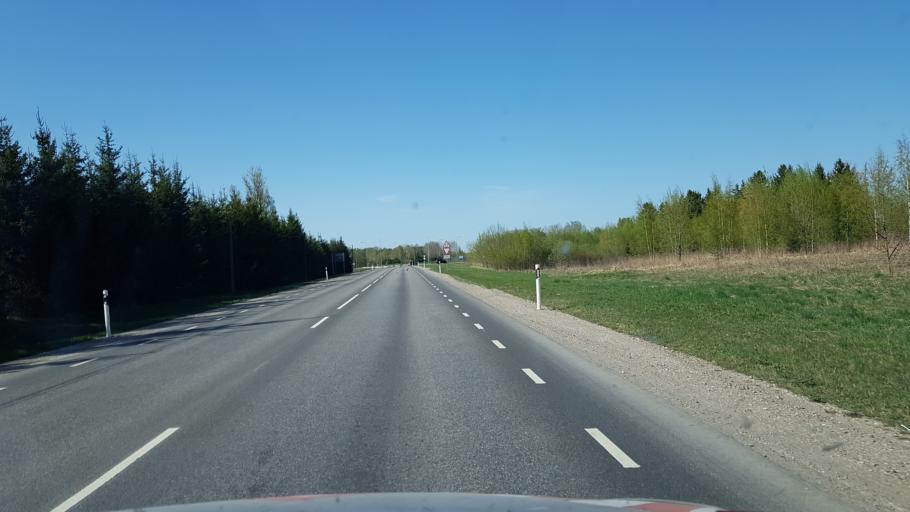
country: EE
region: Viljandimaa
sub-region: Viljandi linn
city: Viljandi
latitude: 58.3531
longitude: 25.5605
